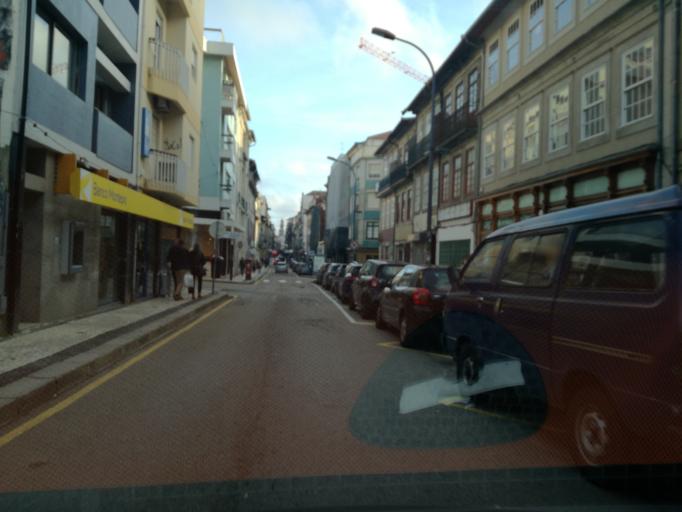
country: PT
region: Porto
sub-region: Porto
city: Porto
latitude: 41.1527
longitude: -8.6181
